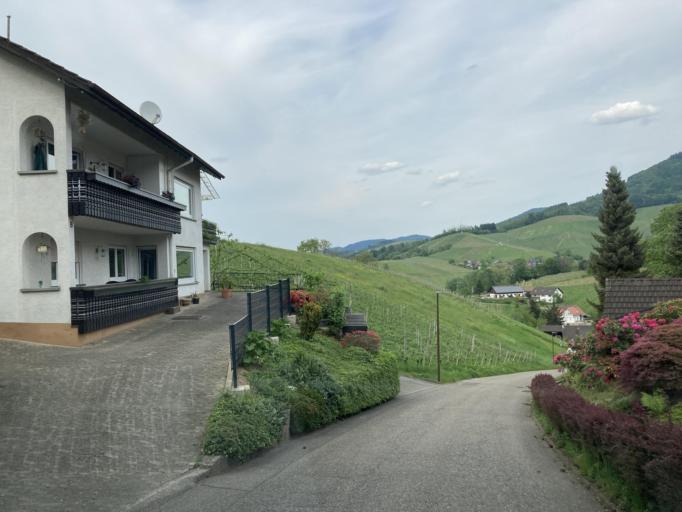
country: DE
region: Baden-Wuerttemberg
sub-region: Freiburg Region
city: Sasbachwalden
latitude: 48.6169
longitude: 8.1110
